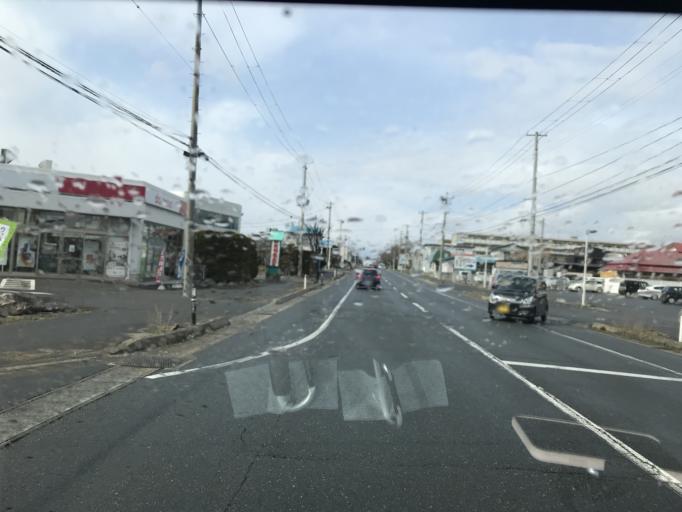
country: JP
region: Iwate
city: Kitakami
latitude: 39.3085
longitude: 141.1146
